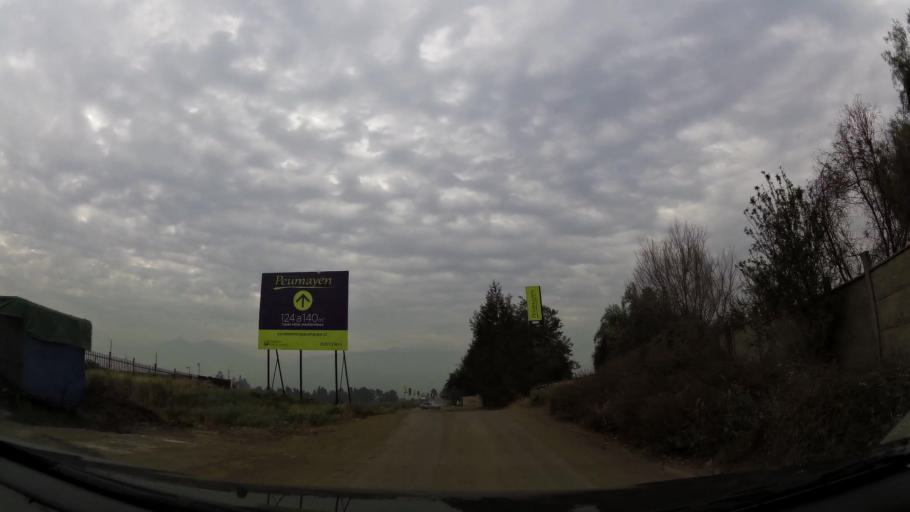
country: CL
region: Santiago Metropolitan
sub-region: Provincia de Chacabuco
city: Chicureo Abajo
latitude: -33.2275
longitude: -70.6759
